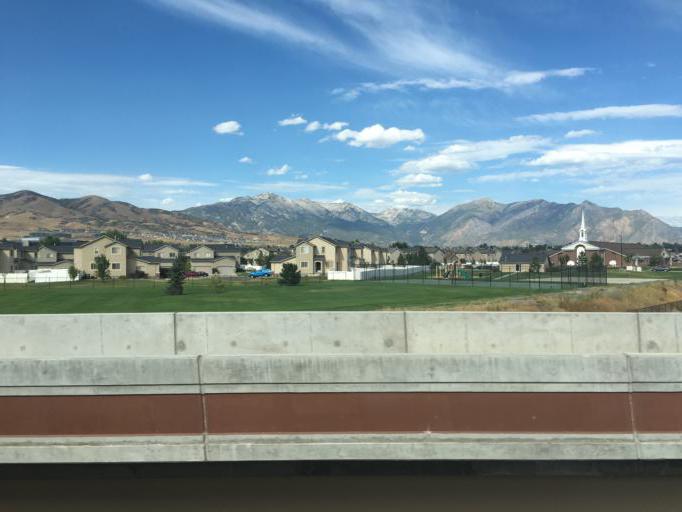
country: US
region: Utah
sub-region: Utah County
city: Lehi
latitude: 40.4132
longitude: -111.8828
